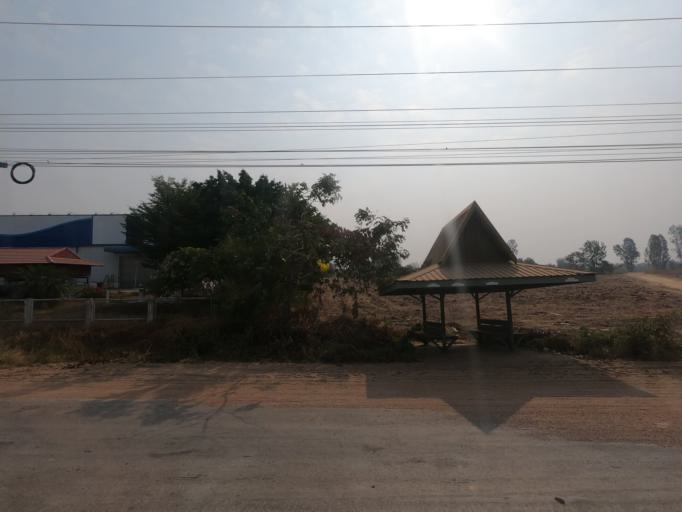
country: TH
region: Khon Kaen
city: Ban Haet
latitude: 16.2334
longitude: 102.7677
